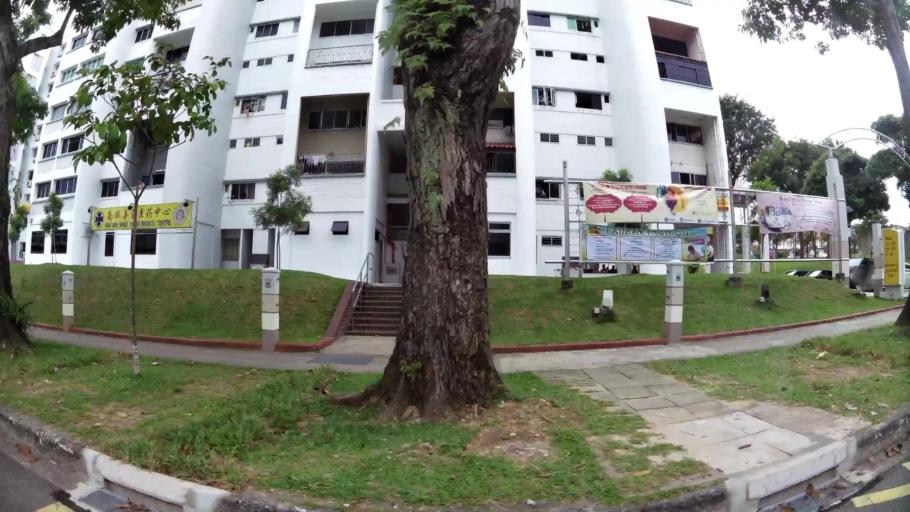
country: SG
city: Singapore
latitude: 1.3587
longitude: 103.8874
